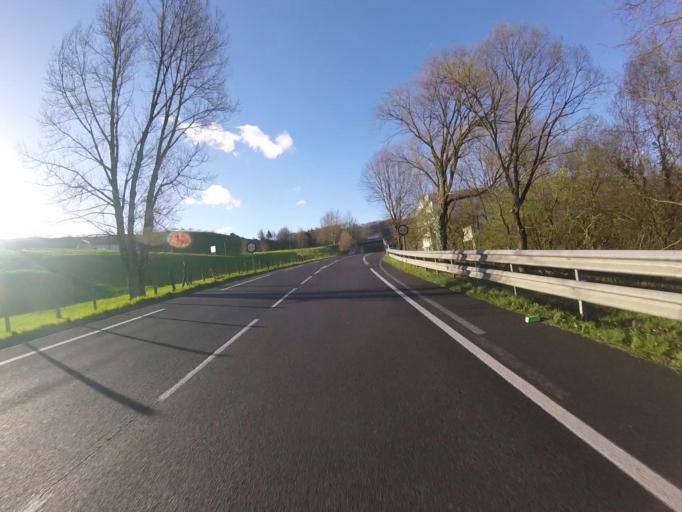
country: ES
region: Basque Country
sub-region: Provincia de Guipuzcoa
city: Errenteria
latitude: 43.2962
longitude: -1.8807
